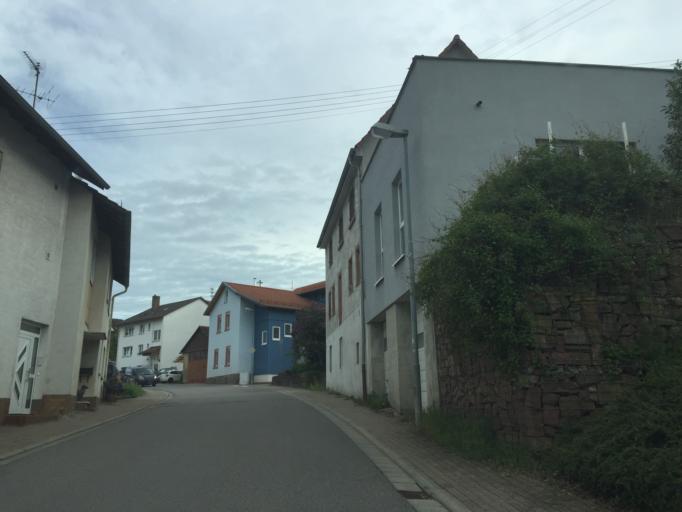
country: DE
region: Hesse
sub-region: Regierungsbezirk Darmstadt
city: Birkenau
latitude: 49.5076
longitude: 8.7078
